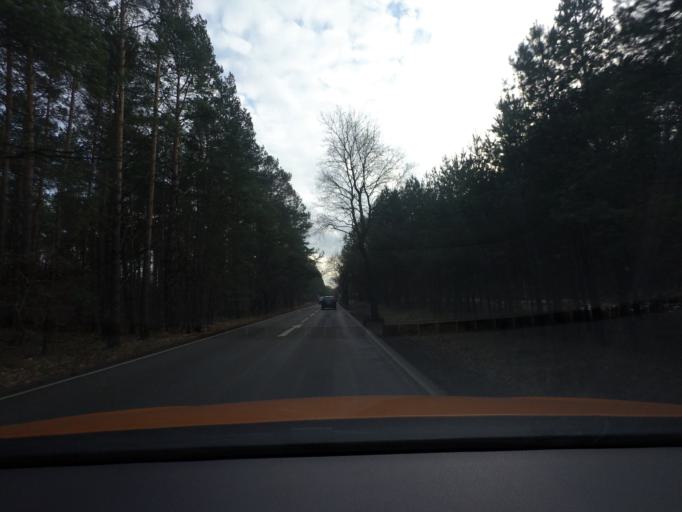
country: DE
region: Brandenburg
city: Birkenwerder
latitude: 52.7172
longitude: 13.3670
